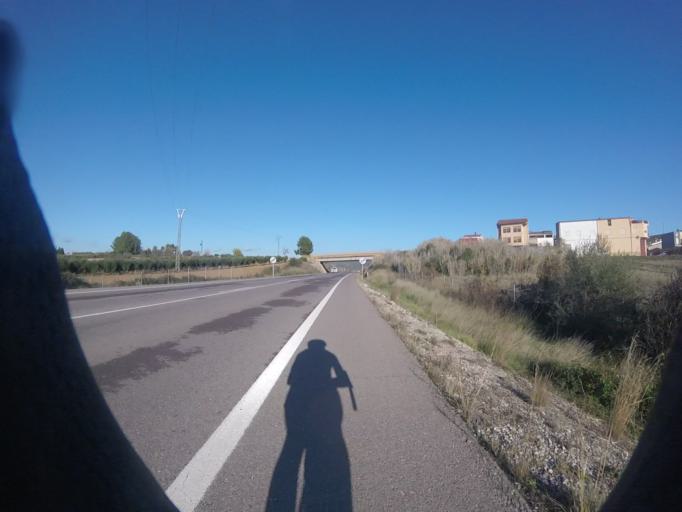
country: ES
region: Valencia
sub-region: Provincia de Castello
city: Cuevas de Vinroma
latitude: 40.3107
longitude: 0.1162
